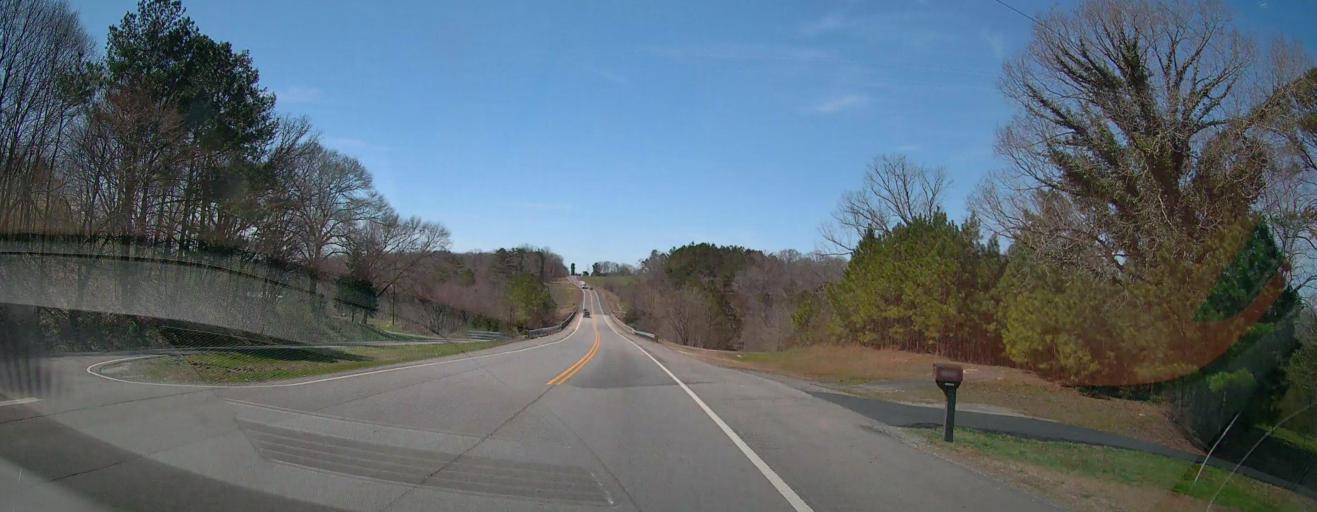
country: US
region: Alabama
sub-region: Blount County
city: Blountsville
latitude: 34.1739
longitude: -86.5591
